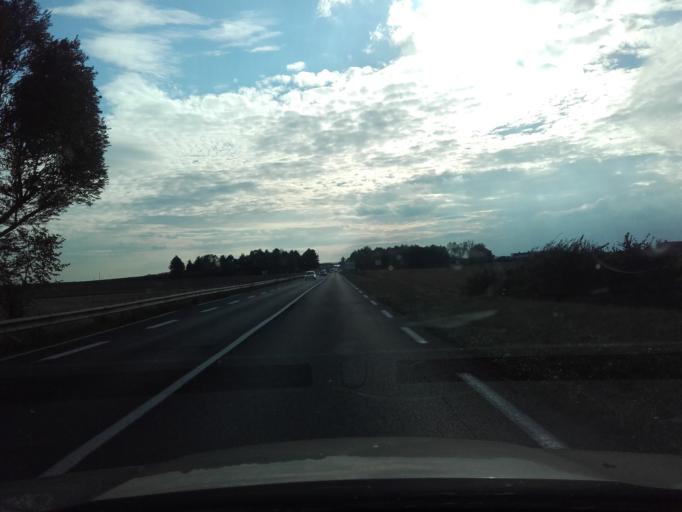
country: FR
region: Centre
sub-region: Departement d'Indre-et-Loire
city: Parcay-Meslay
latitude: 47.4573
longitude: 0.7376
